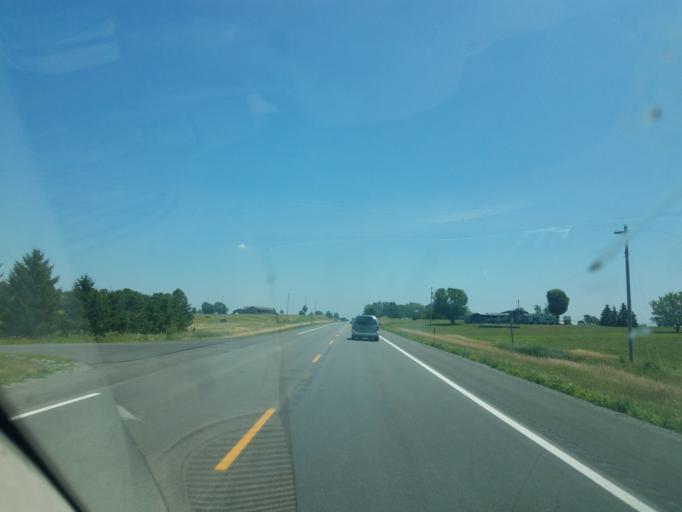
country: US
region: Ohio
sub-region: Hardin County
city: Ada
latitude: 40.7070
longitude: -83.7403
